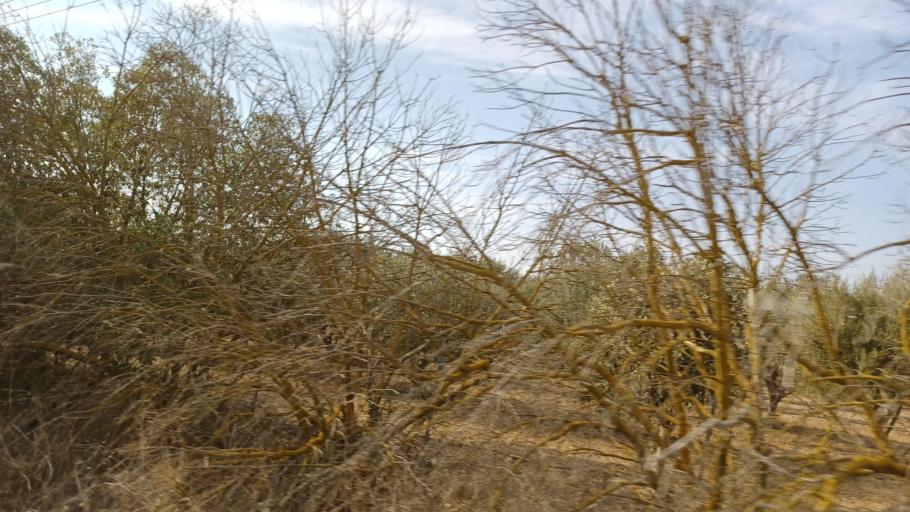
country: CY
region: Ammochostos
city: Frenaros
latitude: 35.0592
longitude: 33.8861
